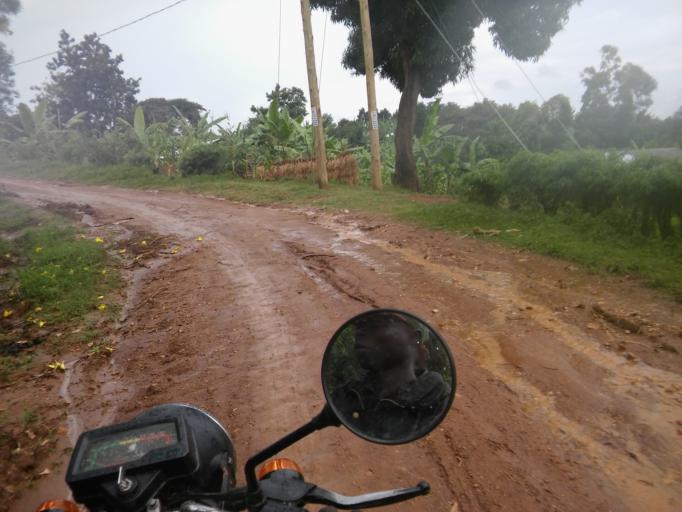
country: UG
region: Eastern Region
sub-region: Bududa District
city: Bududa
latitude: 0.9993
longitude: 34.2431
